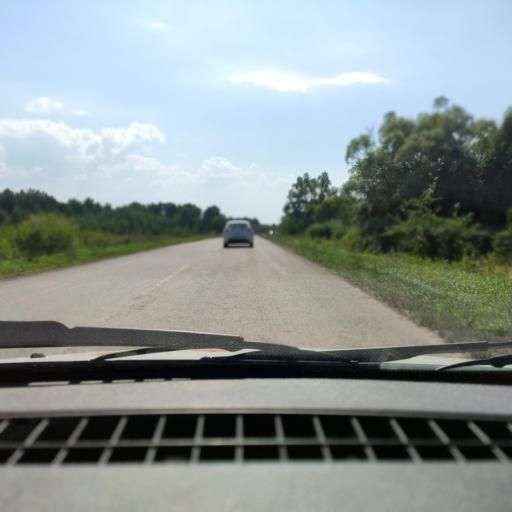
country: RU
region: Bashkortostan
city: Urman
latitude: 54.8605
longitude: 56.8365
